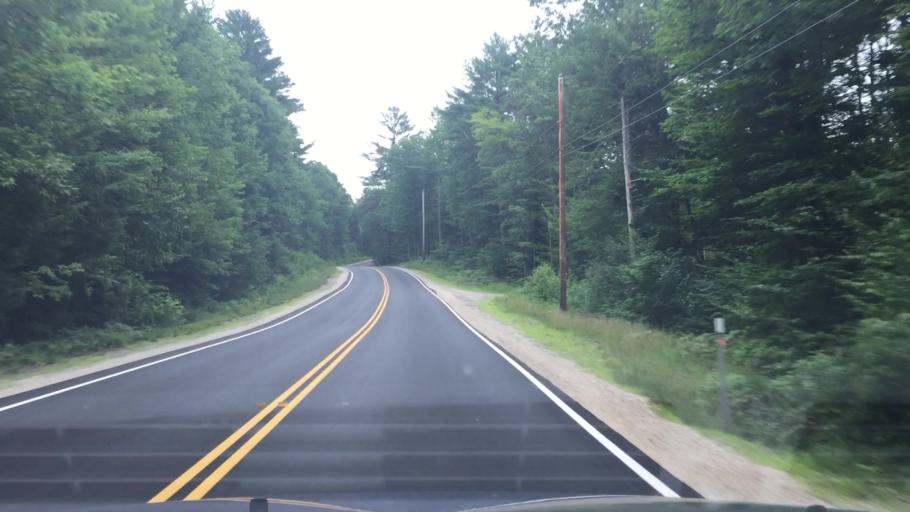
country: US
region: New Hampshire
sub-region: Carroll County
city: Freedom
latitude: 43.8443
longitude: -71.0878
